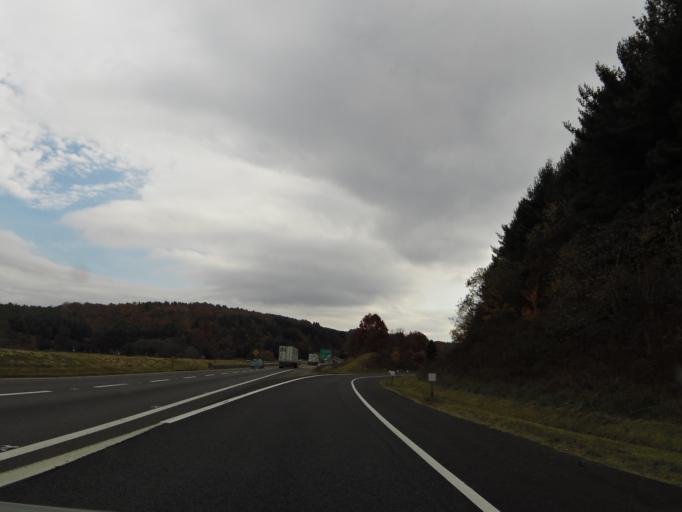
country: US
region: Virginia
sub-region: Carroll County
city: Hillsville
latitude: 36.6772
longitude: -80.7116
